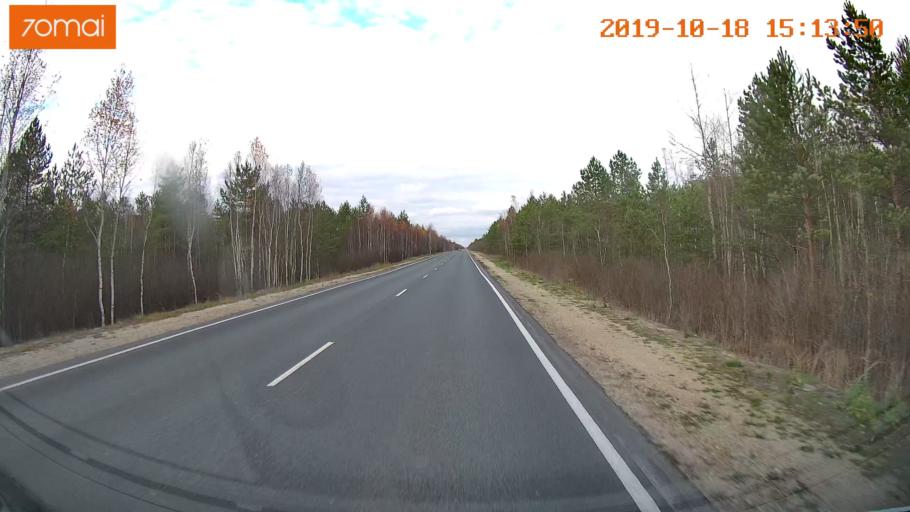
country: RU
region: Vladimir
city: Gus'-Khrustal'nyy
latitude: 55.5930
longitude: 40.7190
